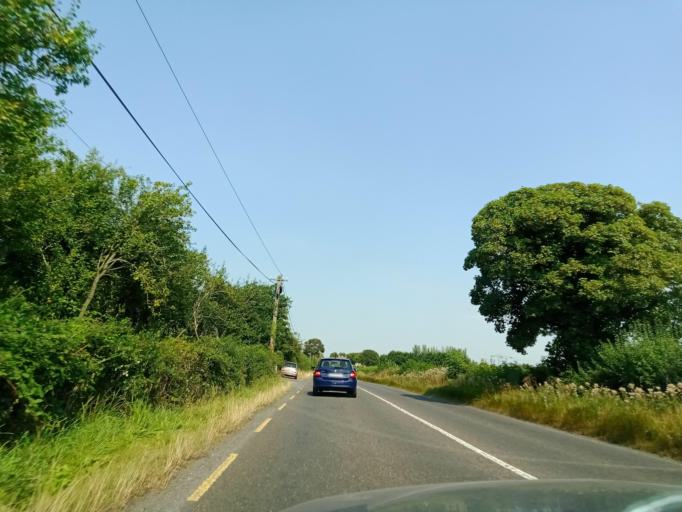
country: IE
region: Leinster
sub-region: Laois
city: Portlaoise
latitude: 53.0593
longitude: -7.2313
